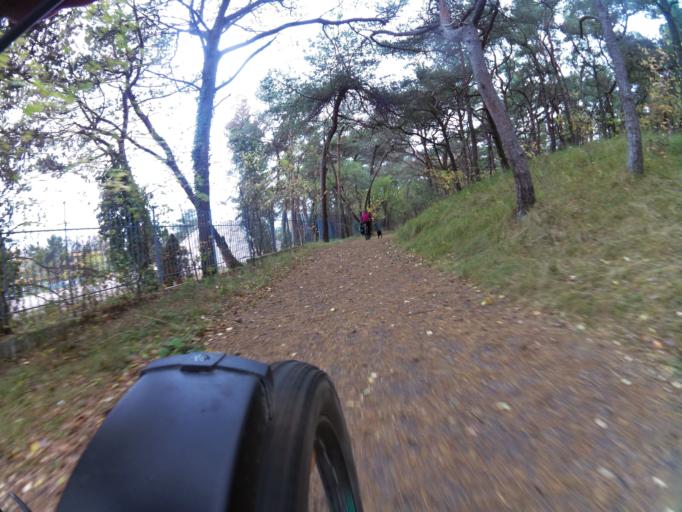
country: PL
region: Pomeranian Voivodeship
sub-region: Powiat pucki
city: Jastarnia
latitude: 54.6932
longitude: 18.6953
